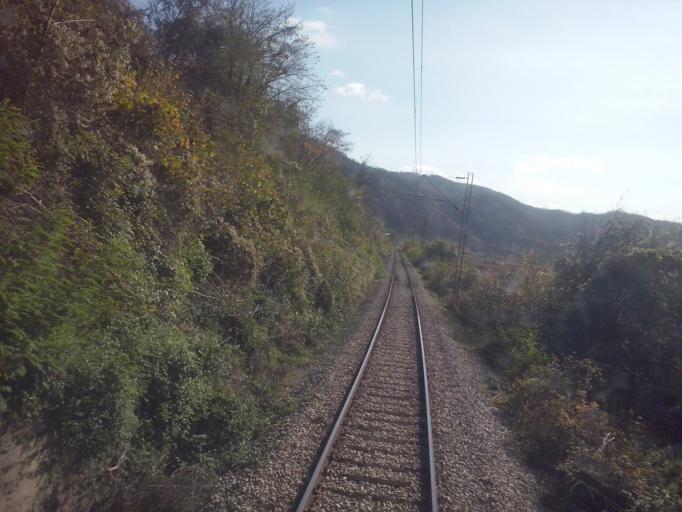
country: RS
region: Central Serbia
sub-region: Zlatiborski Okrug
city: Pozega
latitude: 43.9147
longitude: 19.9943
